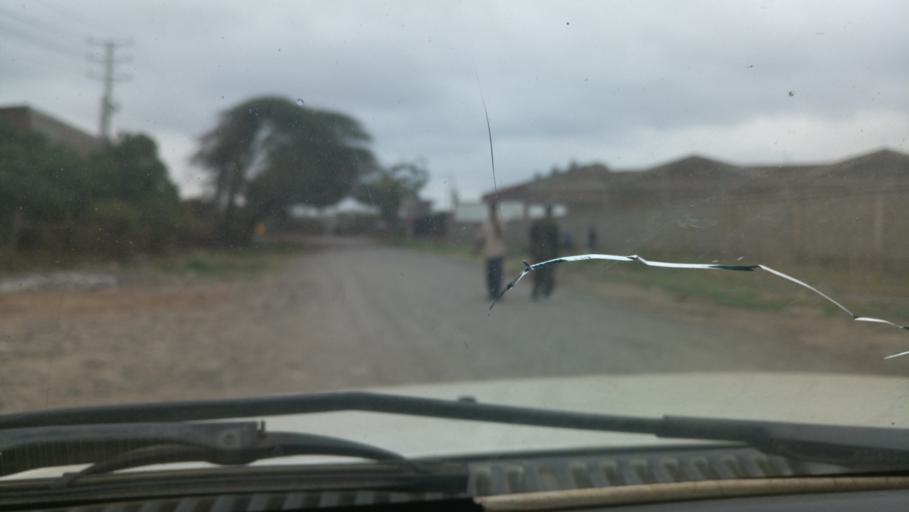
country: KE
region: Nairobi Area
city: Pumwani
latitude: -1.3364
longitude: 36.8658
